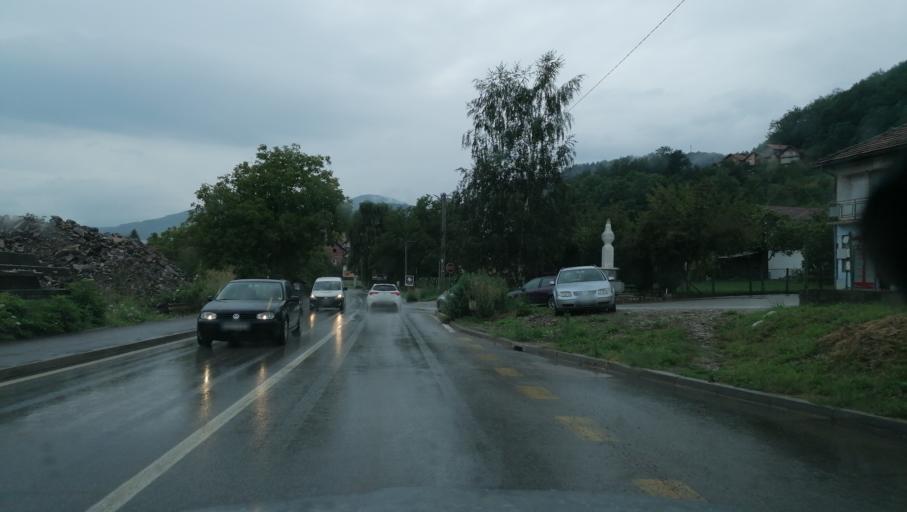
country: BA
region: Federation of Bosnia and Herzegovina
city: Gorazde
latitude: 43.6797
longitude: 18.9894
